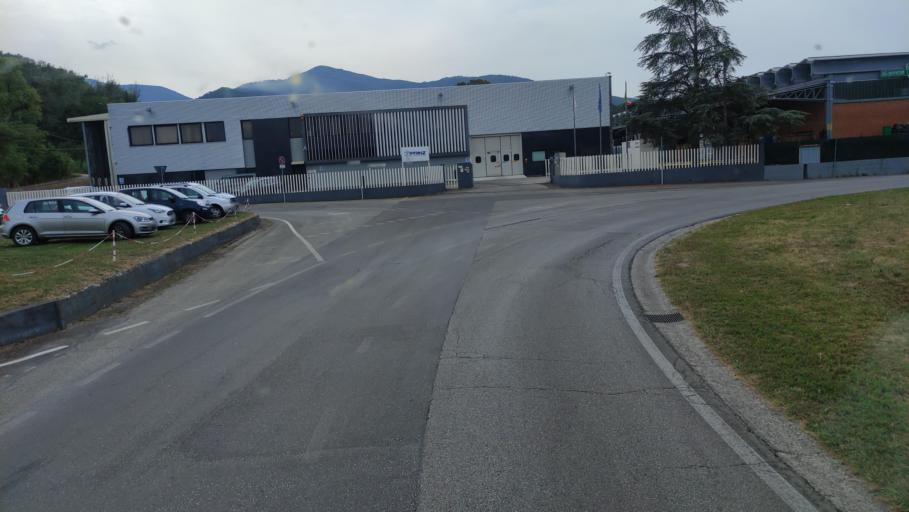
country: IT
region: Tuscany
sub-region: Provincia di Lucca
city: Lucca
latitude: 43.8066
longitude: 10.4987
